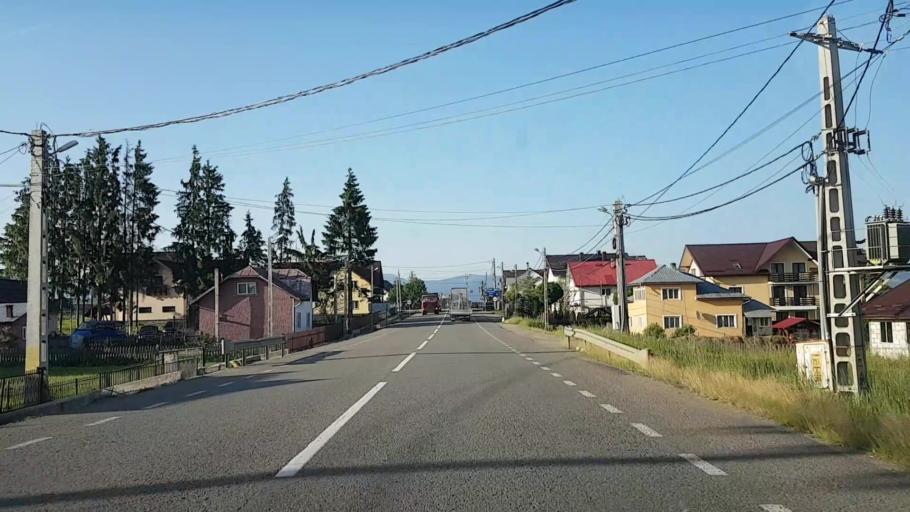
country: RO
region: Suceava
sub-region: Comuna Poiana Stampei
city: Poiana Stampei
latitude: 47.3218
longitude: 25.1380
